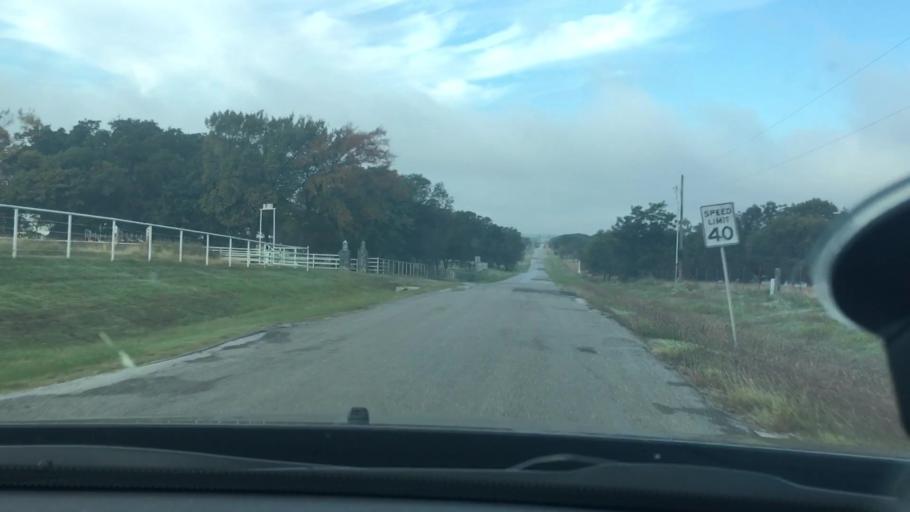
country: US
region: Oklahoma
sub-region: Murray County
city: Sulphur
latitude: 34.6223
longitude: -96.9581
